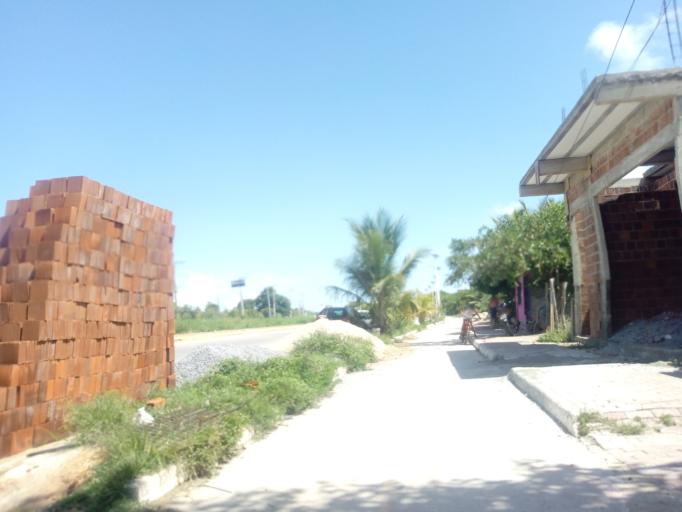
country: BR
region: Pernambuco
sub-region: Ipojuca
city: Ipojuca
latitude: -8.5117
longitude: -35.0094
